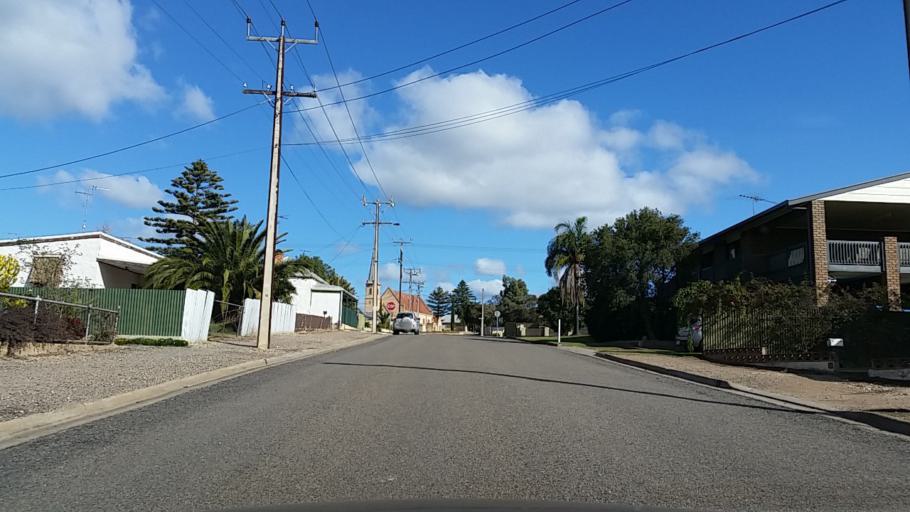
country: AU
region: South Australia
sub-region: Murray Bridge
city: Murray Bridge
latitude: -35.1220
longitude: 139.2772
